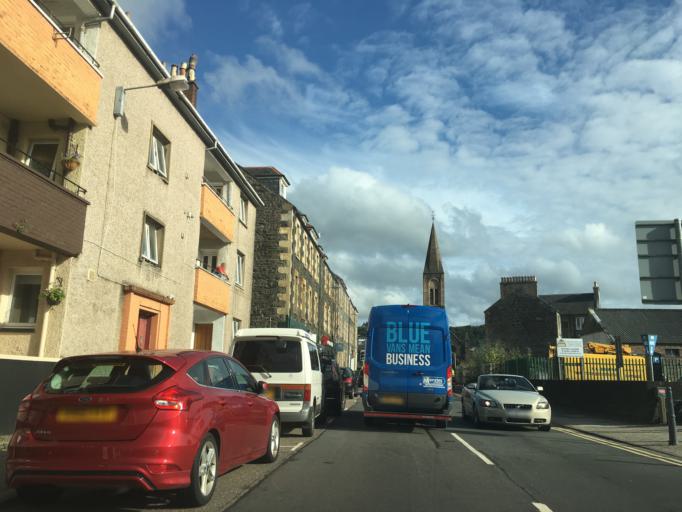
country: GB
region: Scotland
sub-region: Argyll and Bute
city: Oban
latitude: 56.4113
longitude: -5.4703
